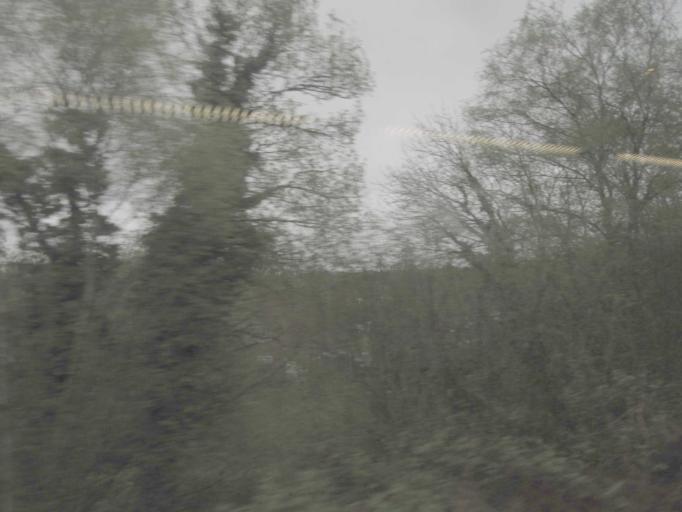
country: GB
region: England
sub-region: Bracknell Forest
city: Sandhurst
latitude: 51.3438
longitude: -0.7987
